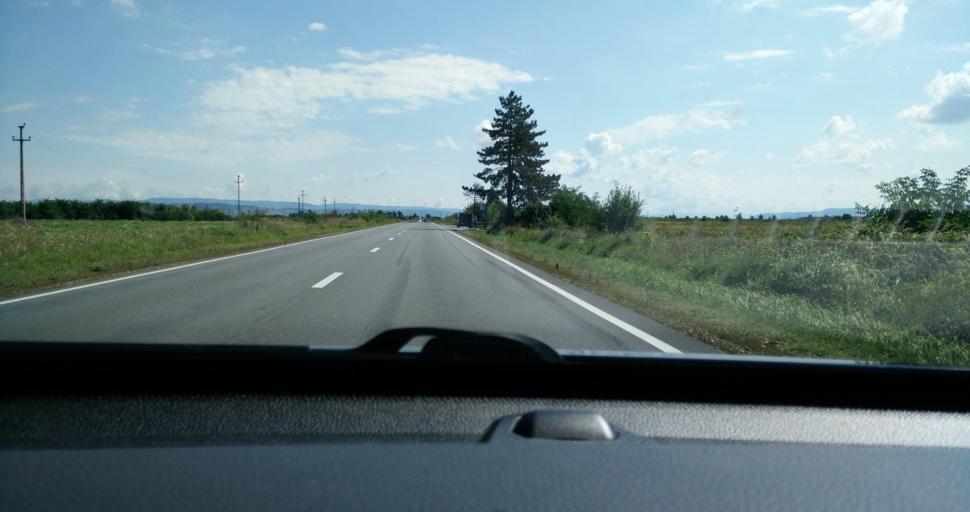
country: RO
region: Bihor
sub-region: Comuna Ineu
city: Ineu
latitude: 47.0586
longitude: 22.1268
